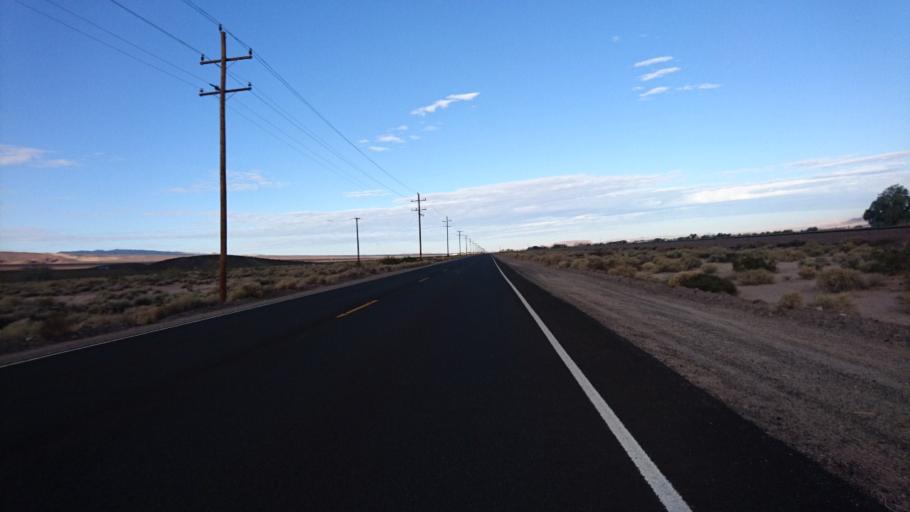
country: US
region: California
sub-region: San Bernardino County
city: Barstow
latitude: 34.8376
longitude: -116.7231
